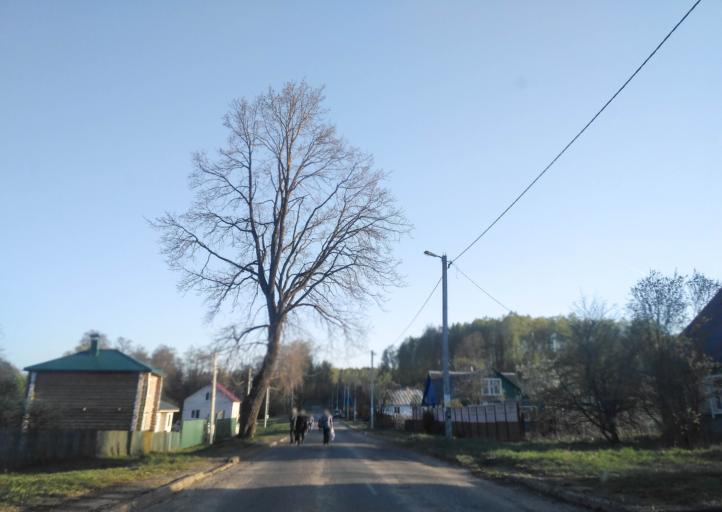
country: BY
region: Minsk
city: Pyatryshki
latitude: 54.0958
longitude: 27.1950
